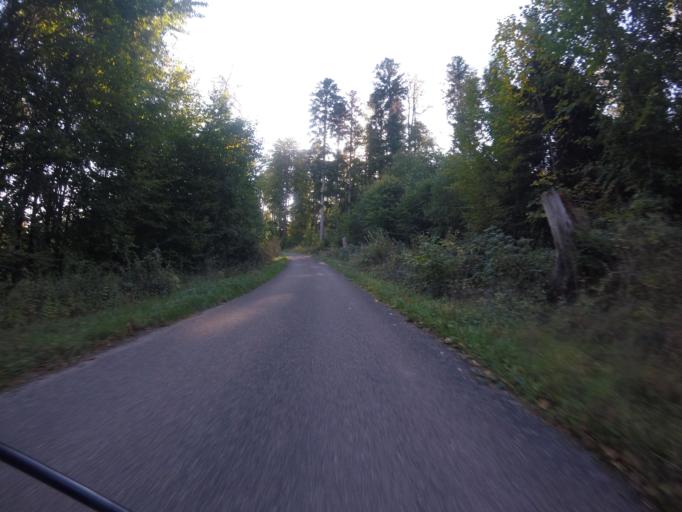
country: DE
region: Baden-Wuerttemberg
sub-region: Regierungsbezirk Stuttgart
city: Spiegelberg
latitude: 49.0095
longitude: 9.4290
